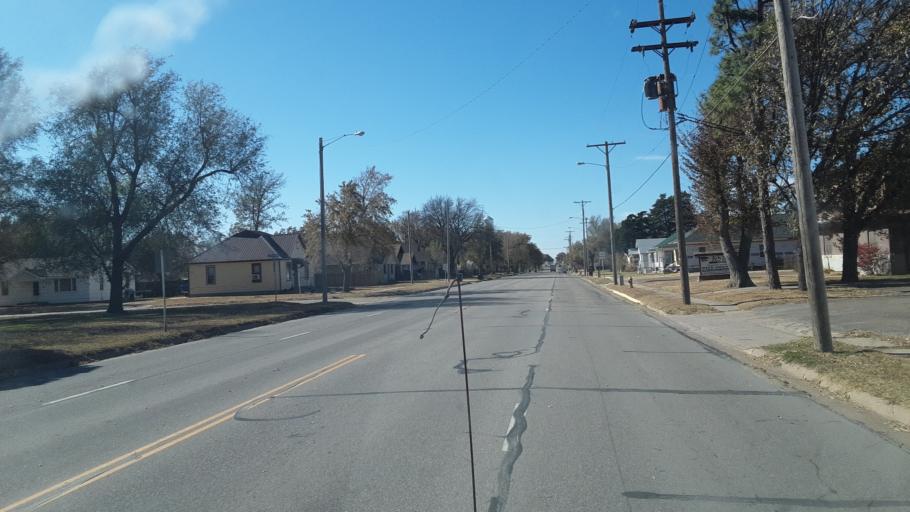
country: US
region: Kansas
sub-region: Rice County
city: Lyons
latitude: 38.3477
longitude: -98.1939
